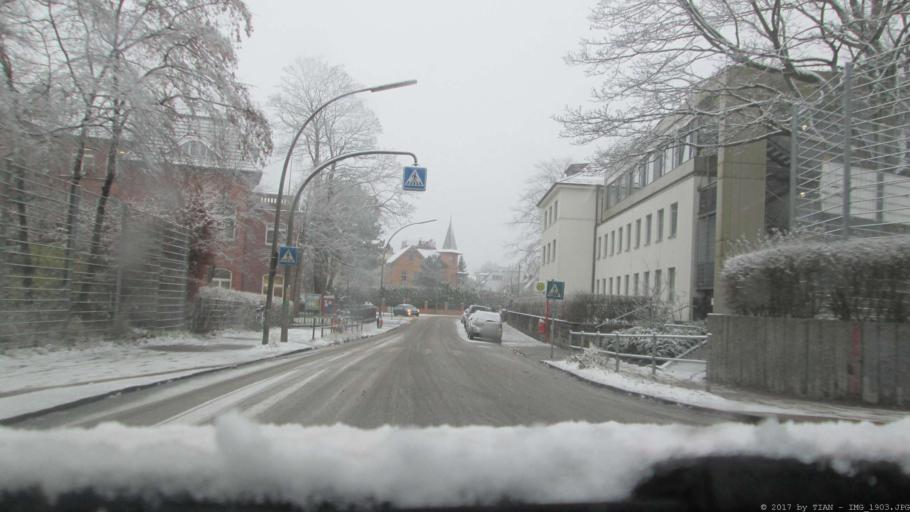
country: DE
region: Schleswig-Holstein
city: Halstenbek
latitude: 53.5626
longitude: 9.8071
